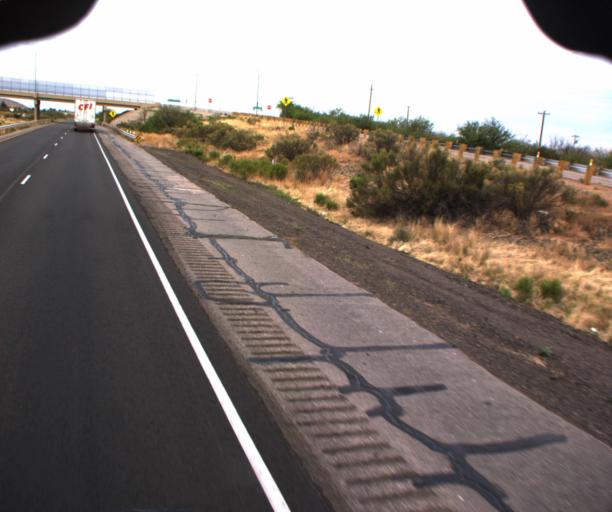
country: US
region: Arizona
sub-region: Cochise County
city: Mescal
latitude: 31.9631
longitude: -110.4328
